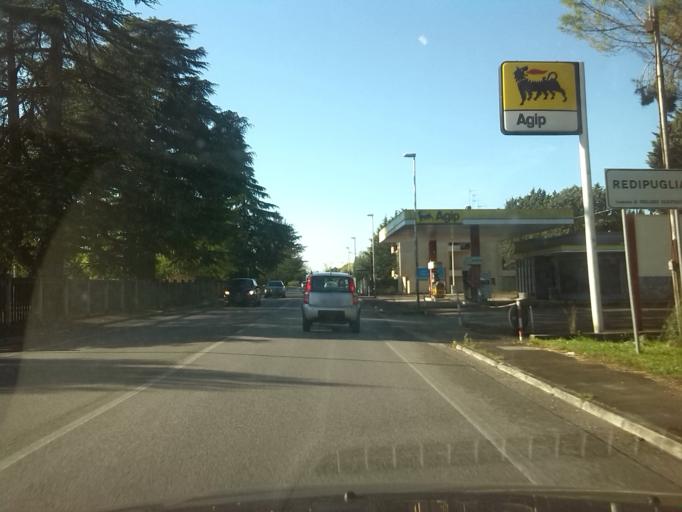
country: IT
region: Friuli Venezia Giulia
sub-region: Provincia di Gorizia
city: Fogliano
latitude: 45.8530
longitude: 13.4857
